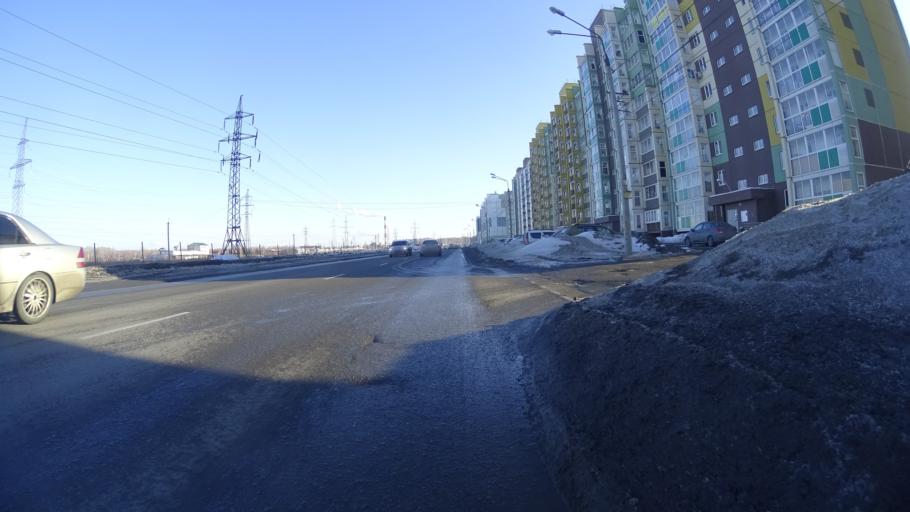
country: RU
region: Chelyabinsk
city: Roshchino
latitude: 55.2174
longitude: 61.3009
